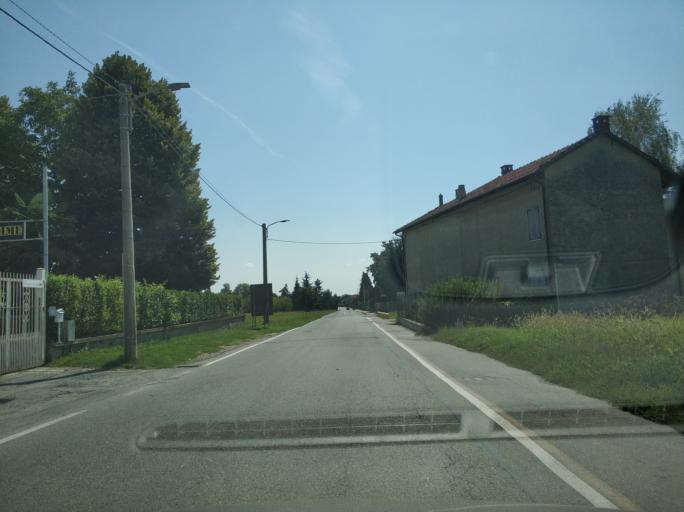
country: IT
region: Piedmont
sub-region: Provincia di Torino
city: San Francesco al Campo
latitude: 45.2346
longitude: 7.6382
